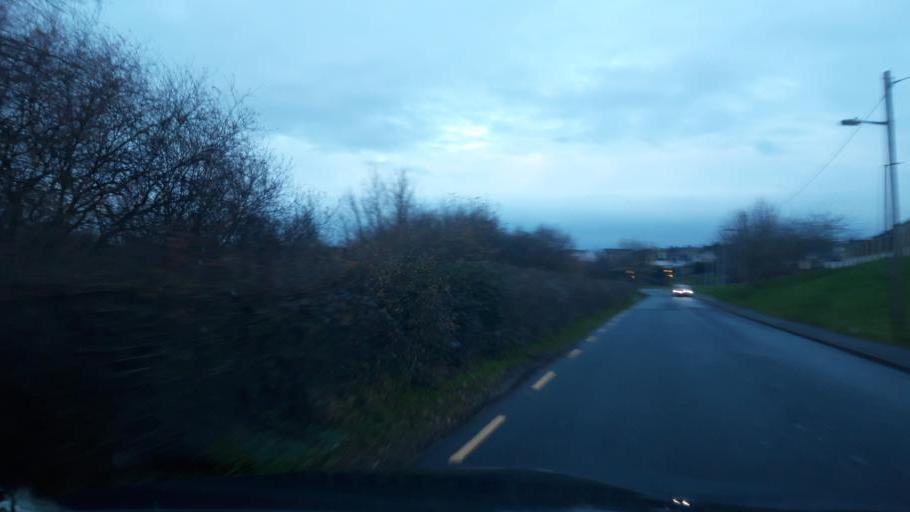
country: IE
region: Leinster
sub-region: Kilkenny
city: Kilkenny
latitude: 52.6627
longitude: -7.2460
